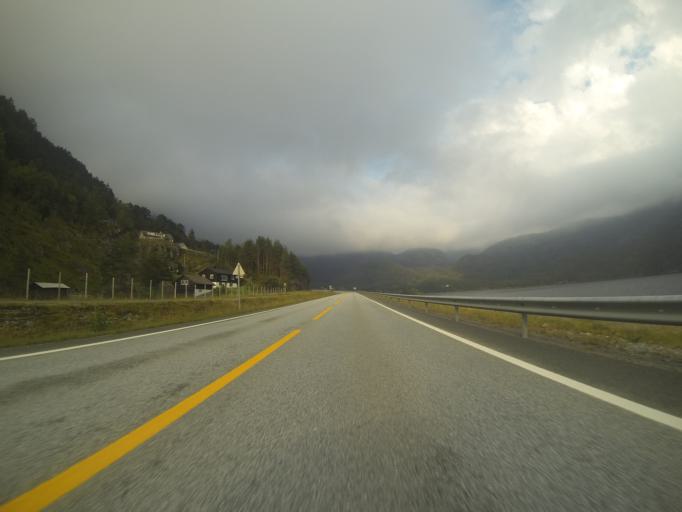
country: NO
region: Rogaland
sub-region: Sauda
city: Sauda
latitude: 59.8743
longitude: 6.4173
